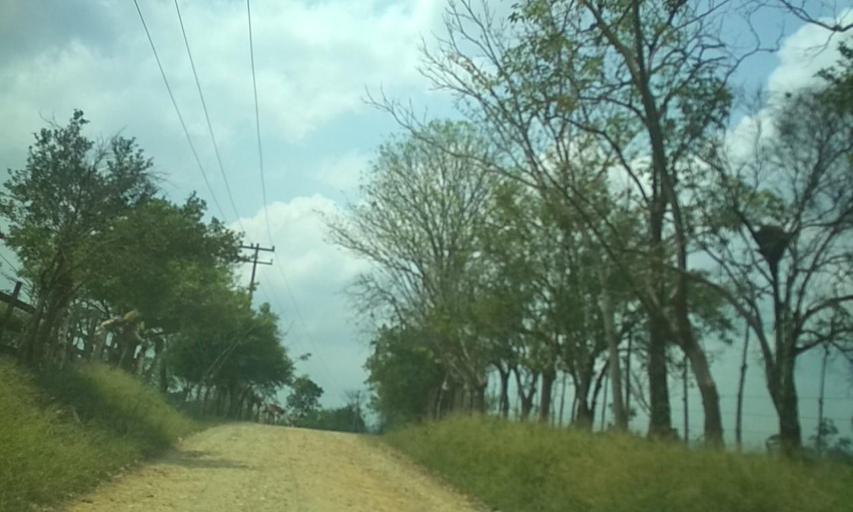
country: MX
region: Tabasco
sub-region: Huimanguillo
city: Francisco Rueda
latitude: 17.5913
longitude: -93.7938
